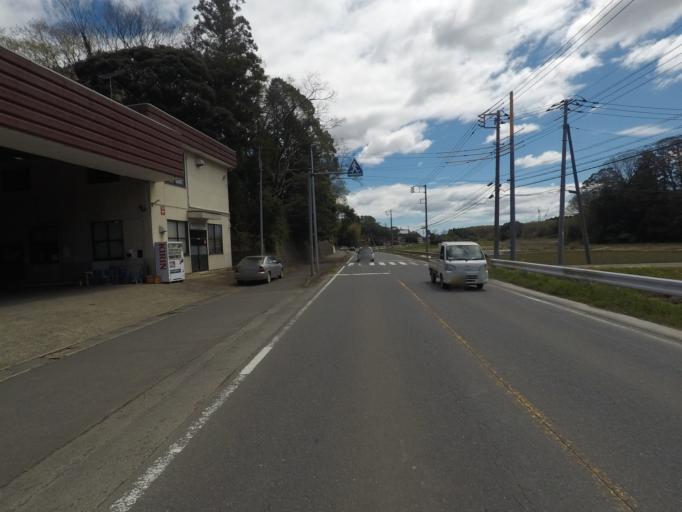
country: JP
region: Ibaraki
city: Okunoya
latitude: 36.1132
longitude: 140.4605
